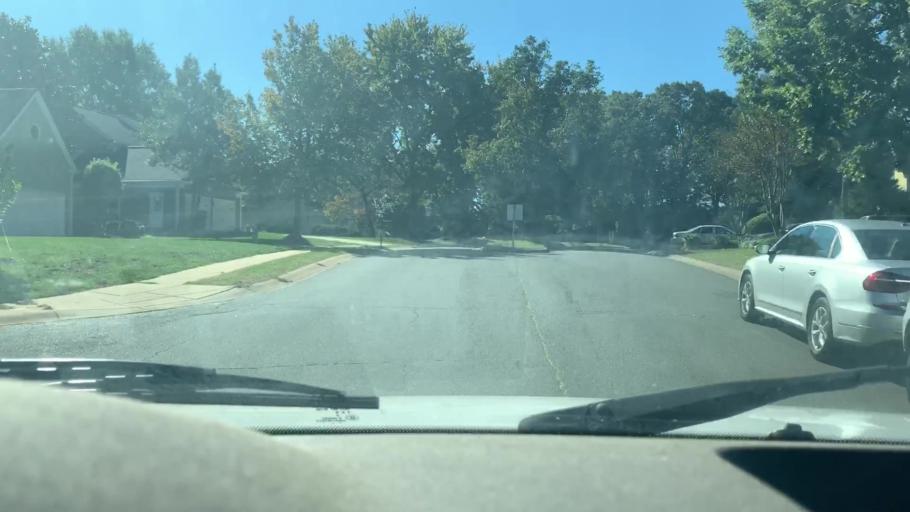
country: US
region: North Carolina
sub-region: Mecklenburg County
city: Charlotte
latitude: 35.2922
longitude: -80.7893
